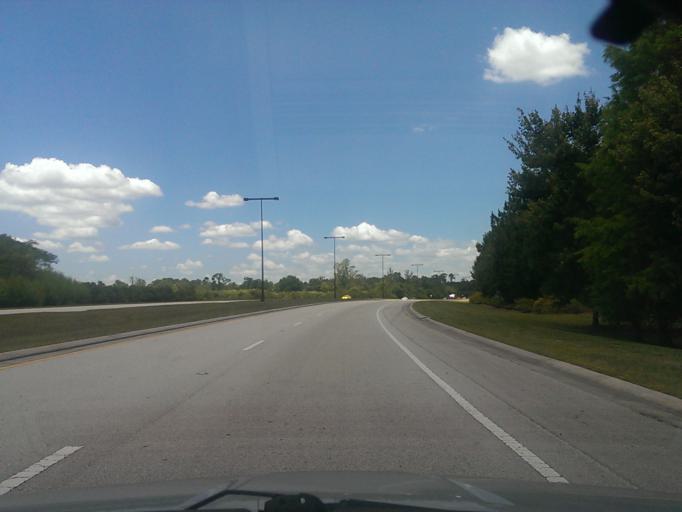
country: US
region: Florida
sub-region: Polk County
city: Citrus Ridge
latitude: 28.3734
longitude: -81.5967
